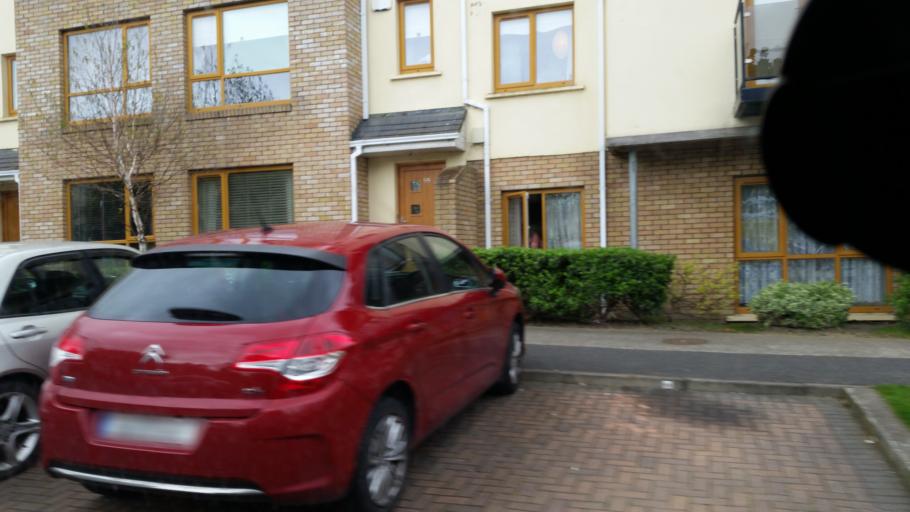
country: IE
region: Leinster
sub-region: Dublin City
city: Finglas
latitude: 53.4049
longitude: -6.2870
